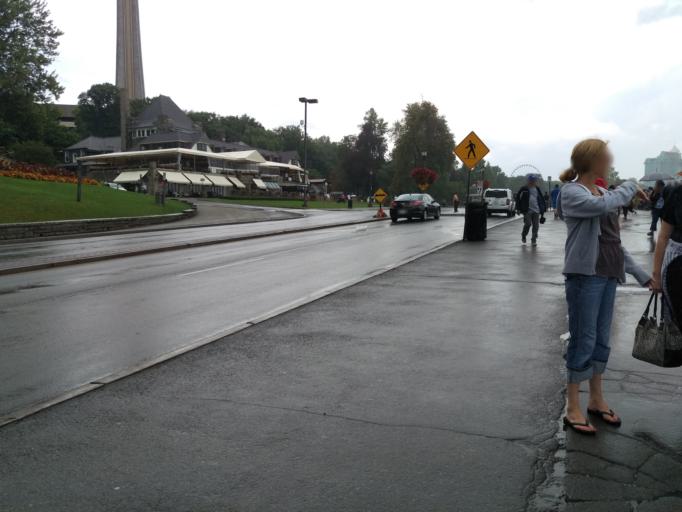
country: CA
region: Ontario
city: Niagara Falls
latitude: 43.0823
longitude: -79.0778
